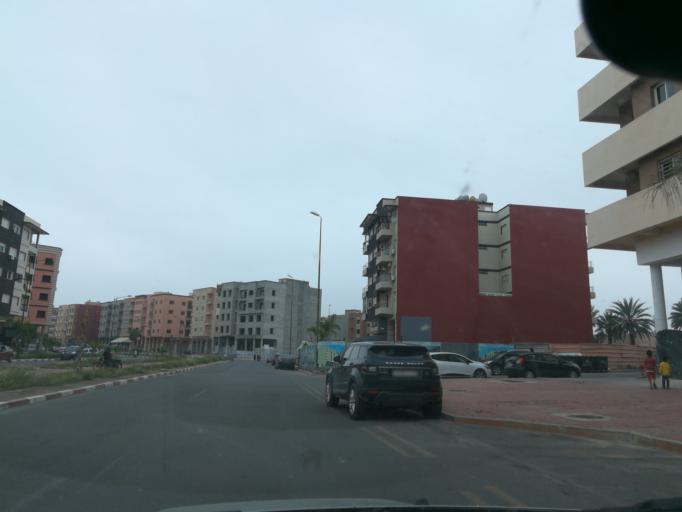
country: MA
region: Marrakech-Tensift-Al Haouz
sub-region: Marrakech
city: Marrakesh
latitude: 31.6745
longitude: -8.0231
